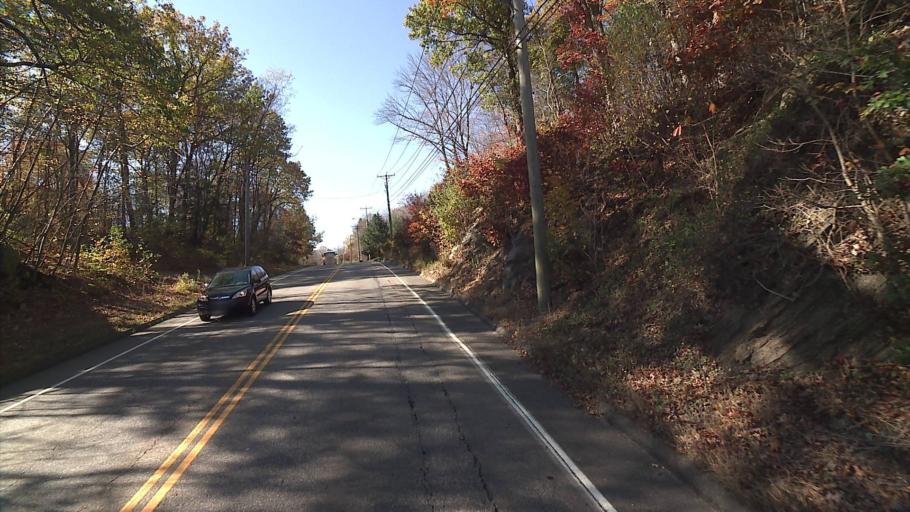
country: US
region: Connecticut
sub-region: Litchfield County
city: Plymouth
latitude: 41.6734
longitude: -73.0451
